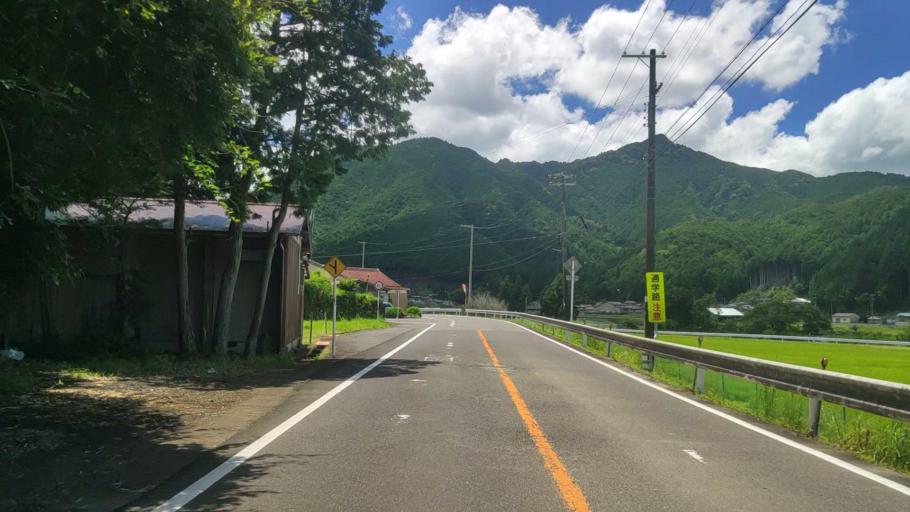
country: JP
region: Mie
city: Owase
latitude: 33.9814
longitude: 136.0493
